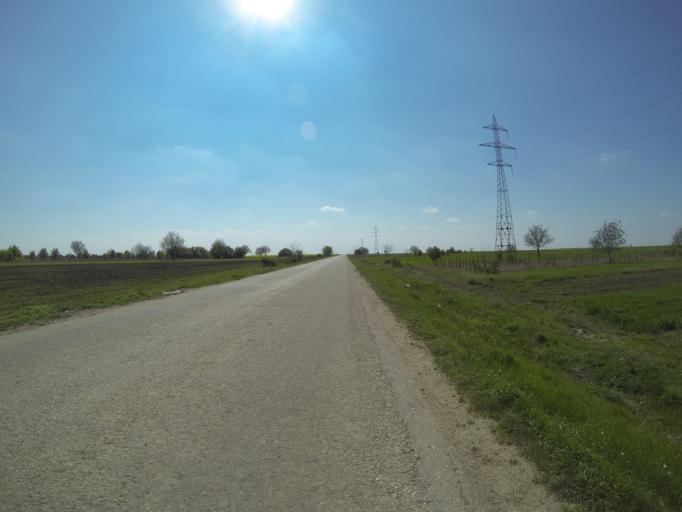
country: RO
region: Dolj
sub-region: Comuna Unirea
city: Unirea
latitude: 44.1670
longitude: 23.1668
